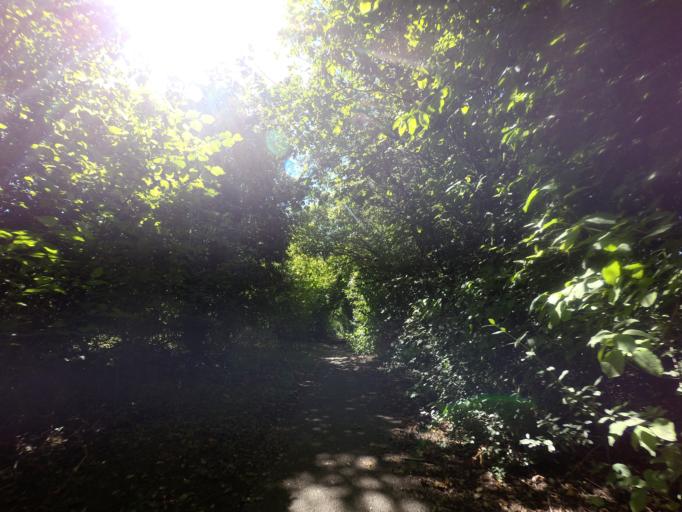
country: GB
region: England
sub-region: Kent
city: Eastry
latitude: 51.2267
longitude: 1.3019
